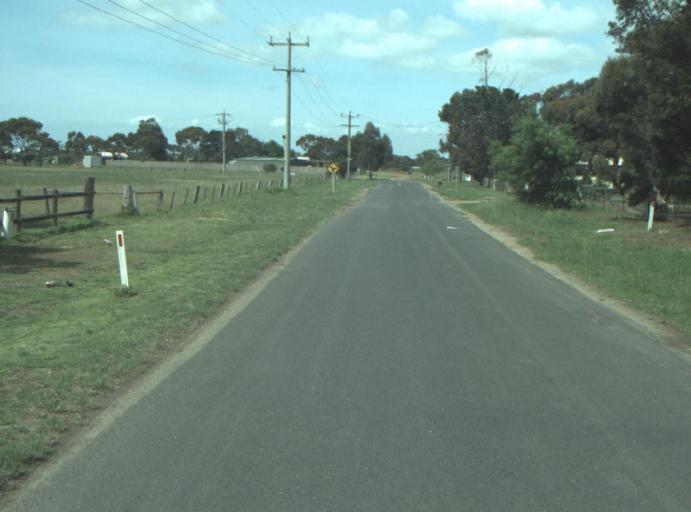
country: AU
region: Victoria
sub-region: Wyndham
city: Little River
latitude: -37.9702
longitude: 144.5065
